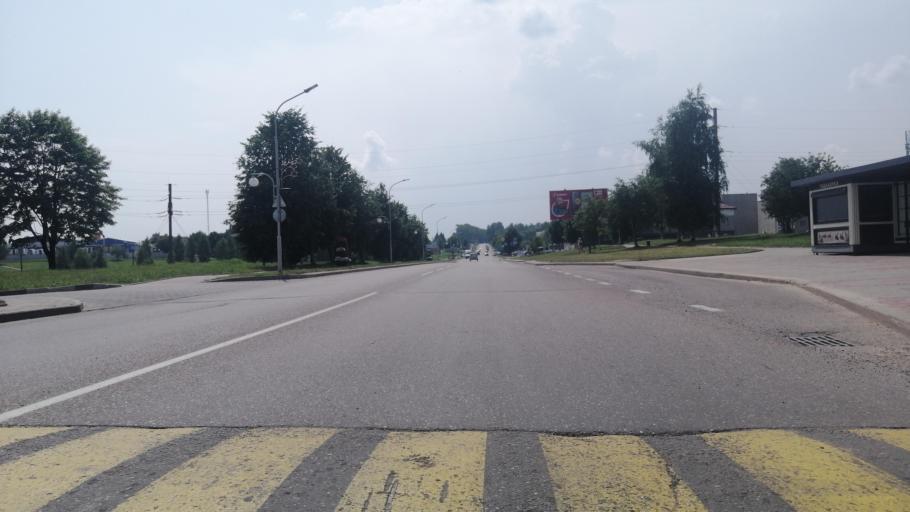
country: BY
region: Grodnenskaya
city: Navahrudak
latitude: 53.5863
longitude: 25.8092
